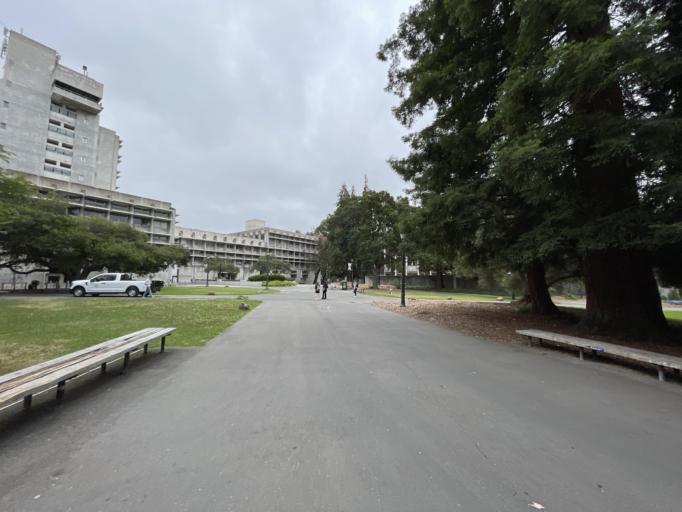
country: US
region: California
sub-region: Alameda County
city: Berkeley
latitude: 37.8708
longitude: -122.2558
